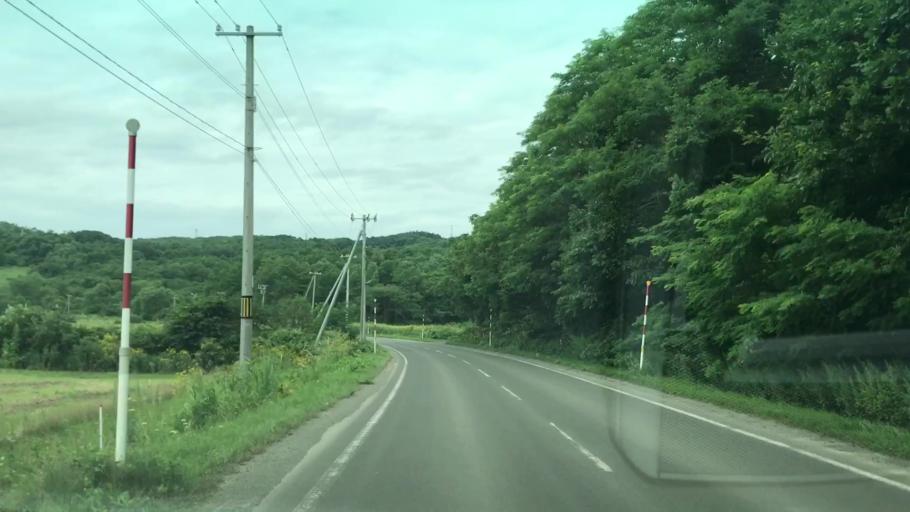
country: JP
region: Hokkaido
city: Iwanai
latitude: 43.0364
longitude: 140.5481
